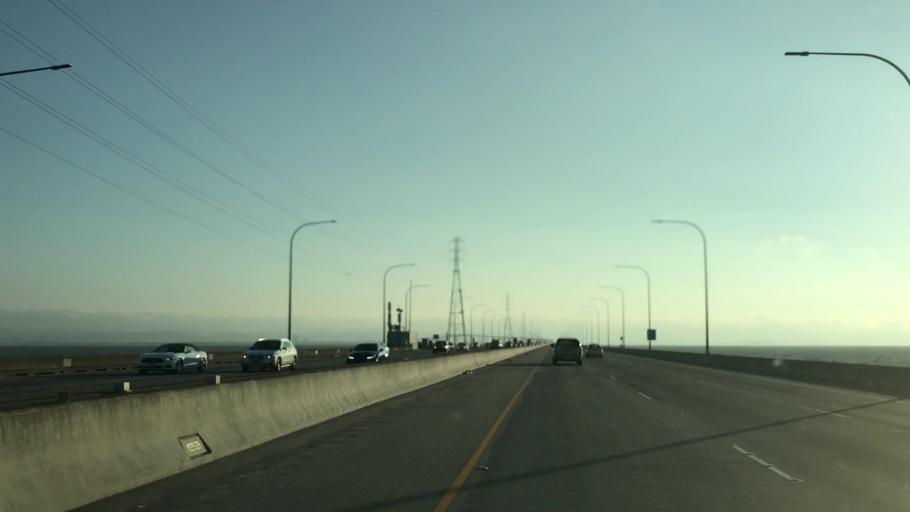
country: US
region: California
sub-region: San Mateo County
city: Foster City
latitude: 37.6039
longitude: -122.2000
